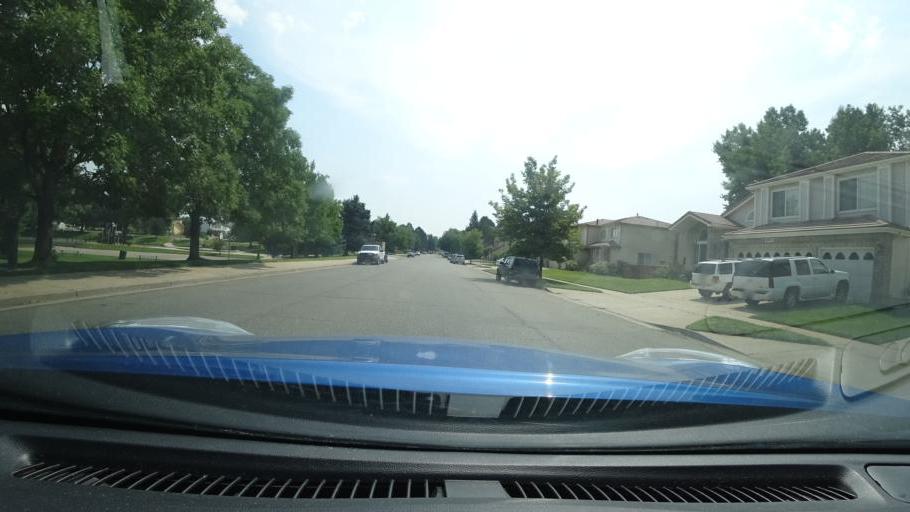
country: US
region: Colorado
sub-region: Adams County
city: Aurora
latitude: 39.7780
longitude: -104.7684
